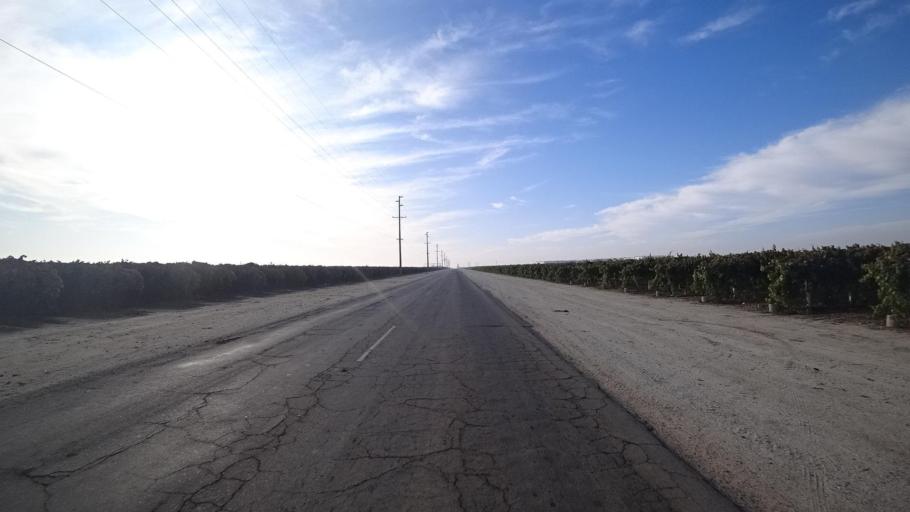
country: US
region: California
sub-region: Kern County
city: McFarland
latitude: 35.7105
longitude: -119.2050
